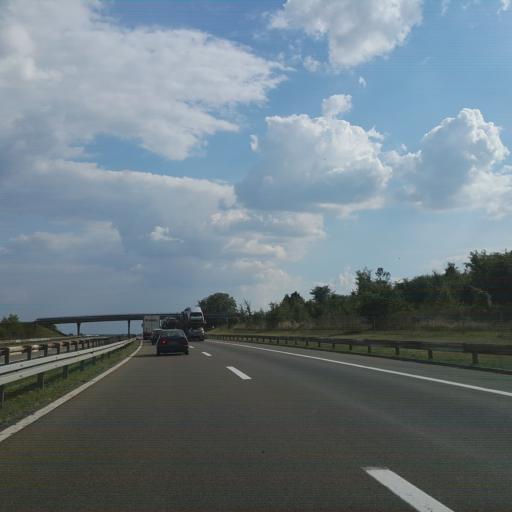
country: RS
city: Lugavcina
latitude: 44.4460
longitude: 21.0465
